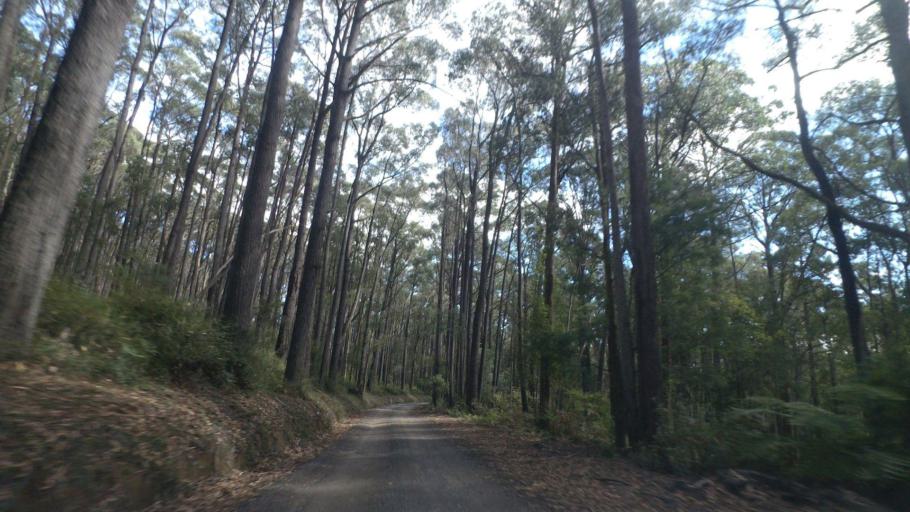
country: AU
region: Victoria
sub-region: Cardinia
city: Gembrook
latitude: -37.9185
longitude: 145.6052
